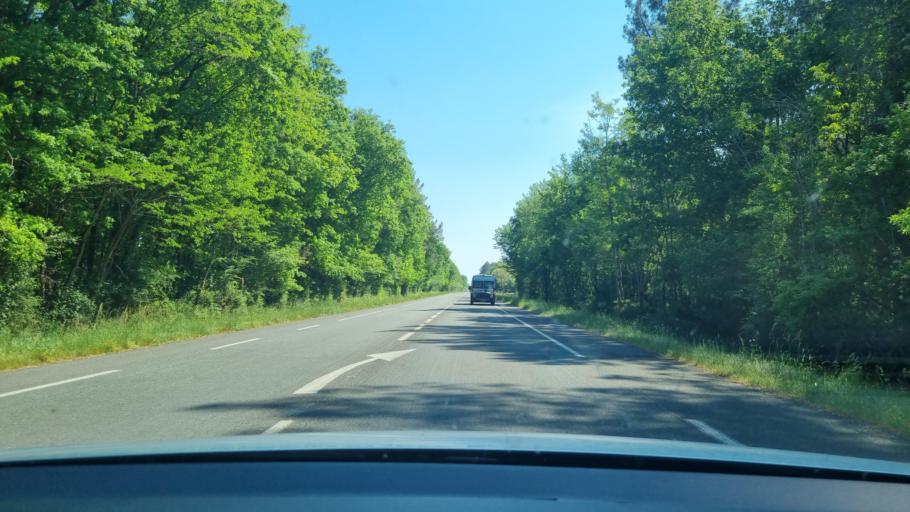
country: FR
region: Aquitaine
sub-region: Departement de la Gironde
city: Prechac
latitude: 44.2658
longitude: -0.2615
